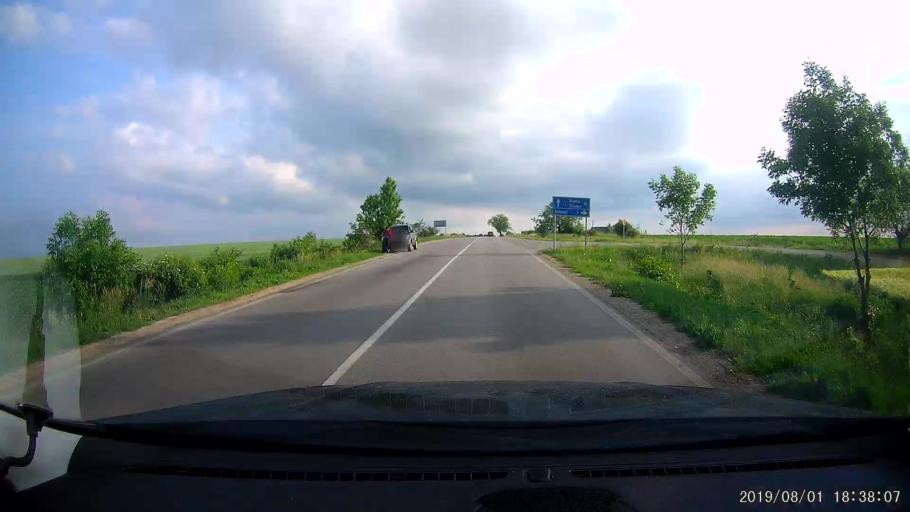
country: BG
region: Shumen
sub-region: Obshtina Khitrino
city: Gara Khitrino
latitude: 43.4074
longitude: 26.9207
